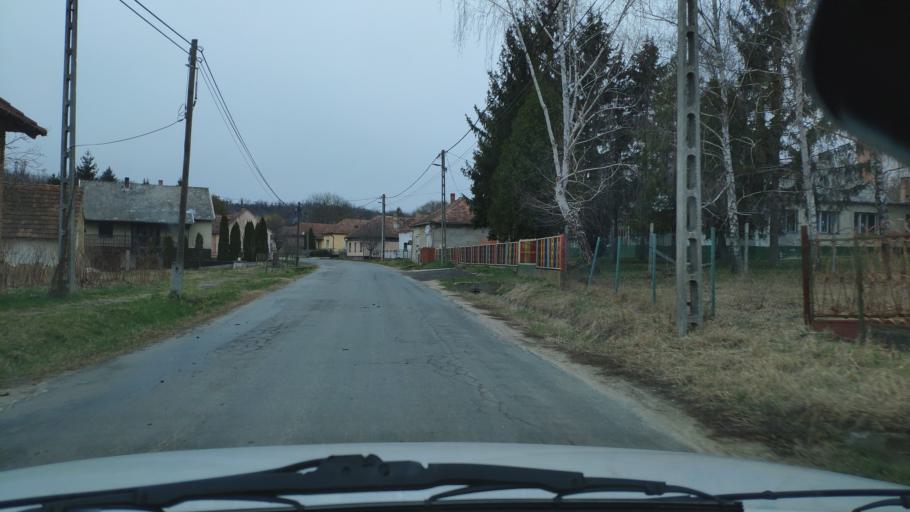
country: HU
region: Zala
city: Pacsa
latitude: 46.6755
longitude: 17.0548
